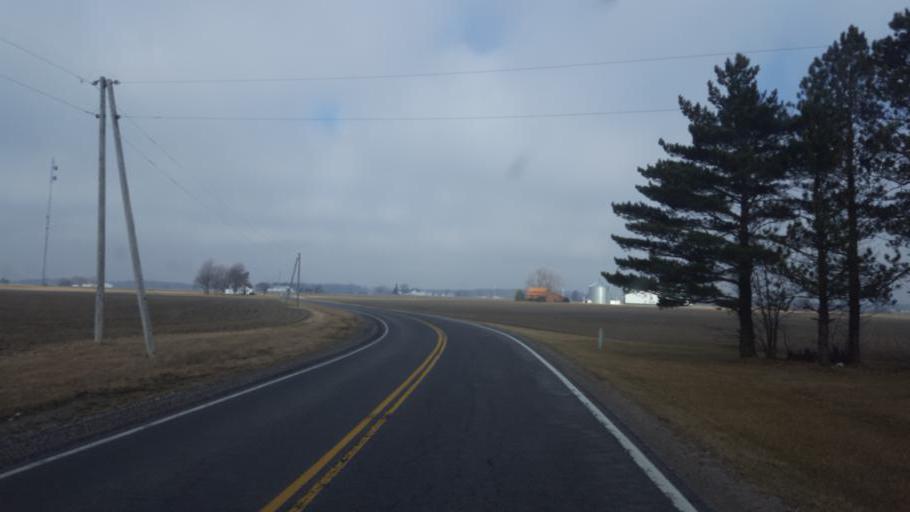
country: US
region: Ohio
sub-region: Crawford County
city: Galion
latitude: 40.7133
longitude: -82.8780
